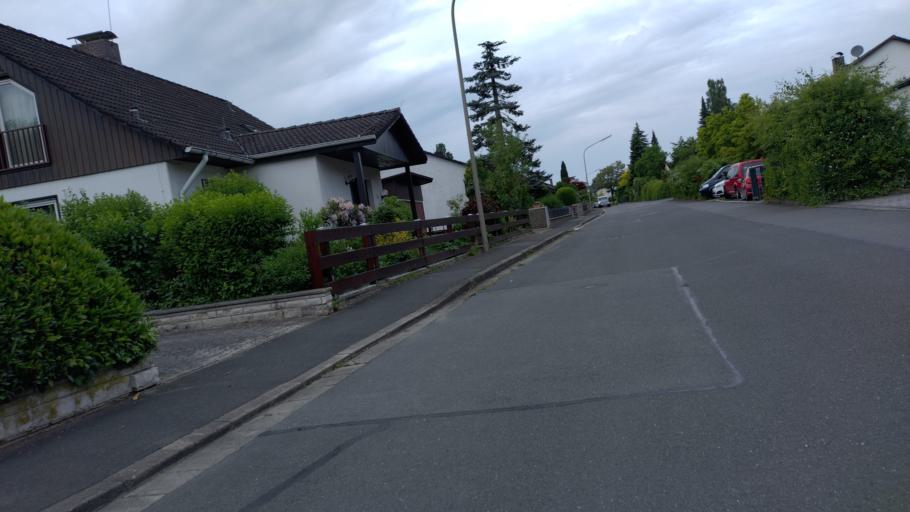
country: DE
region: Bavaria
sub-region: Upper Franconia
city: Bindlach
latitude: 50.0057
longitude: 11.5979
